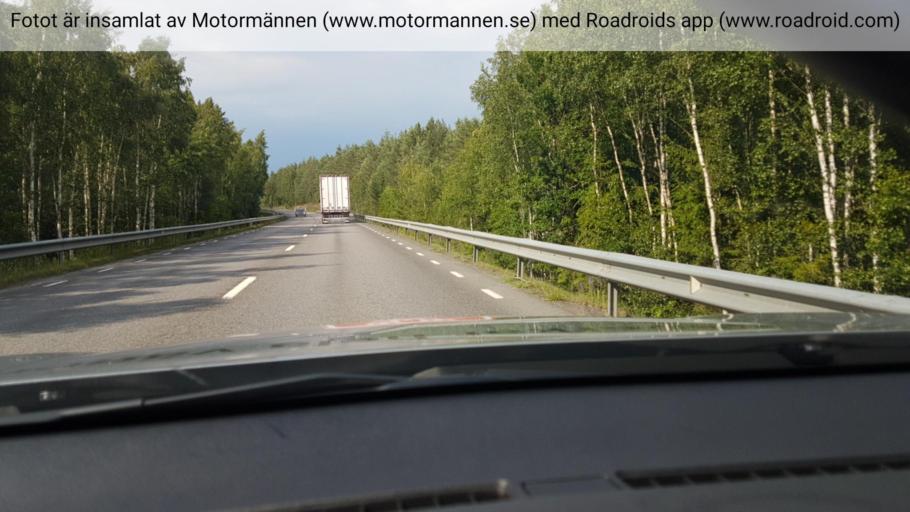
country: SE
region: Joenkoeping
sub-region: Habo Kommun
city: Habo
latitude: 57.9568
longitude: 14.1066
